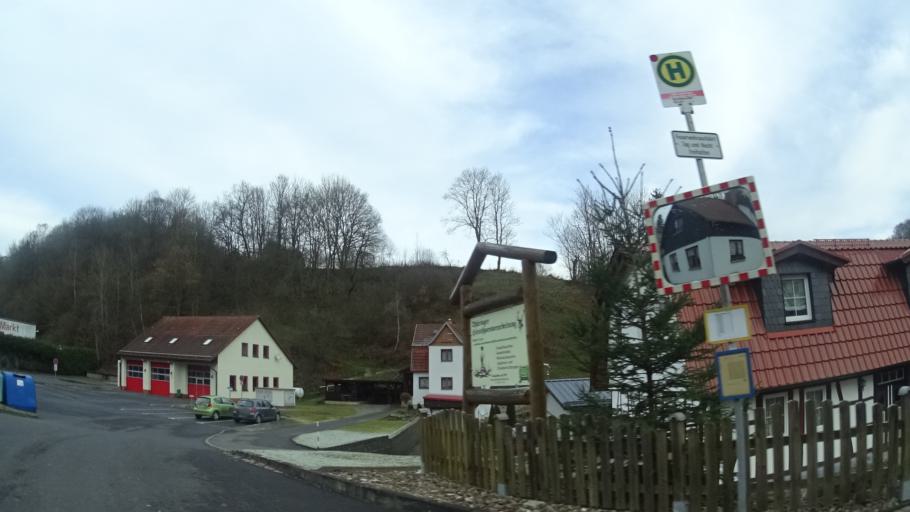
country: DE
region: Thuringia
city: Pappenheim
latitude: 50.7972
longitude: 10.4730
